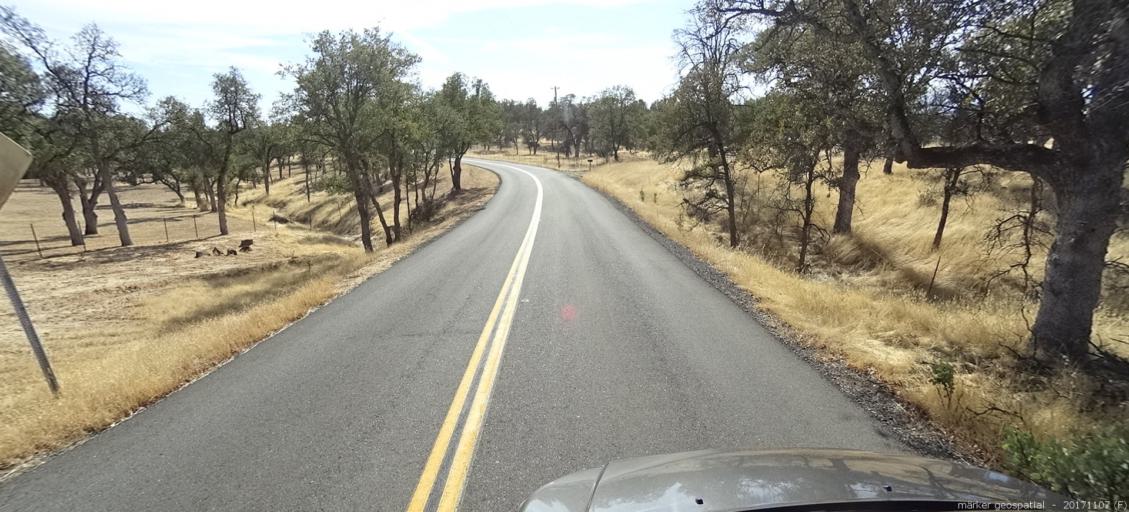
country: US
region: California
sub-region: Shasta County
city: Shasta
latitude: 40.4472
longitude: -122.5308
